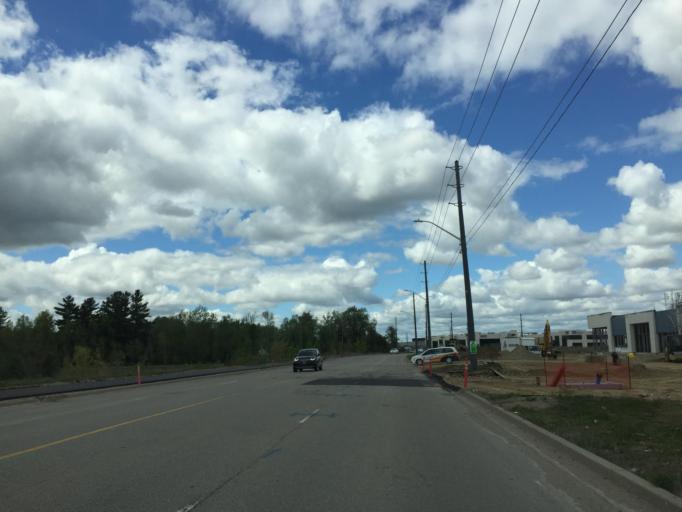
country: CA
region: Ontario
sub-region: Wellington County
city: Guelph
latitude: 43.4871
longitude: -80.2167
